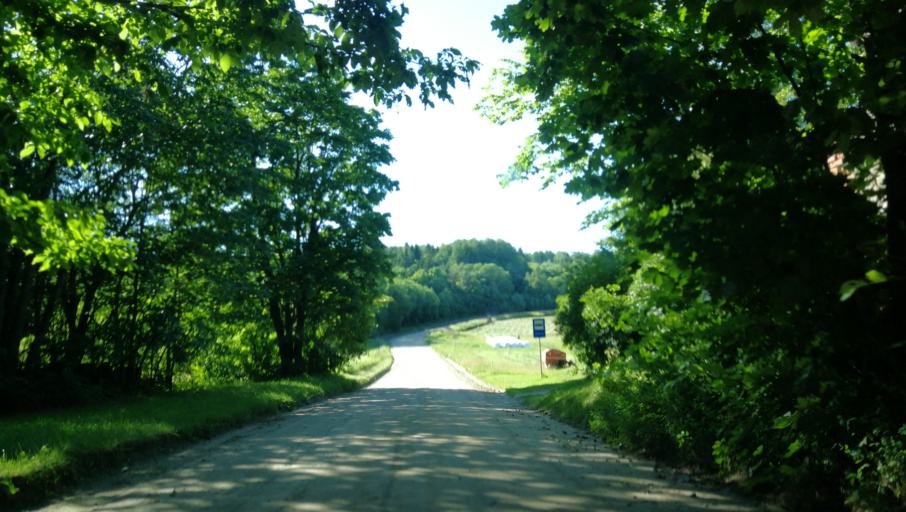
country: LV
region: Jaunpiebalga
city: Jaunpiebalga
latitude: 57.0264
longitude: 26.0254
